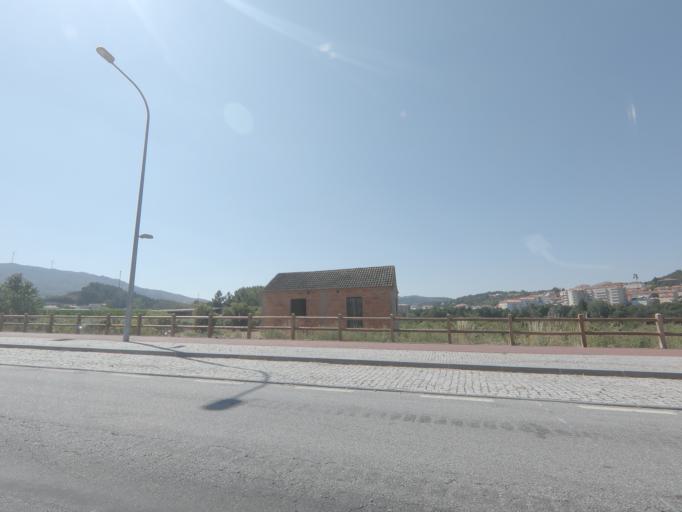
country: PT
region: Viseu
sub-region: Tarouca
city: Tarouca
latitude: 41.0249
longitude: -7.7659
